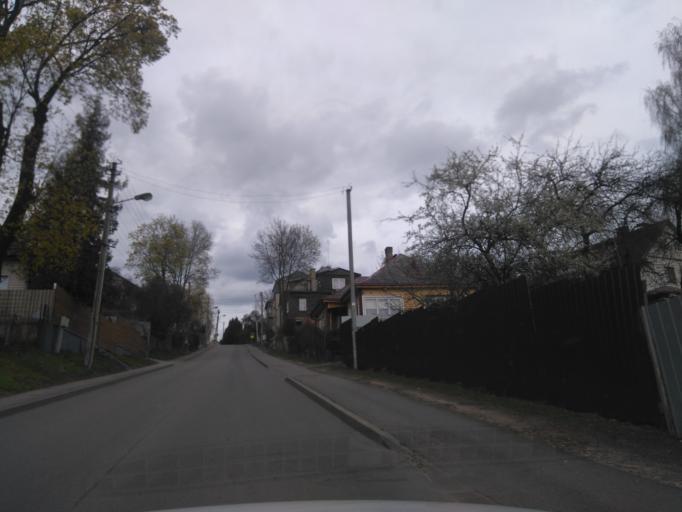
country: LT
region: Kauno apskritis
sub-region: Kaunas
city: Aleksotas
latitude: 54.8758
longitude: 23.9410
